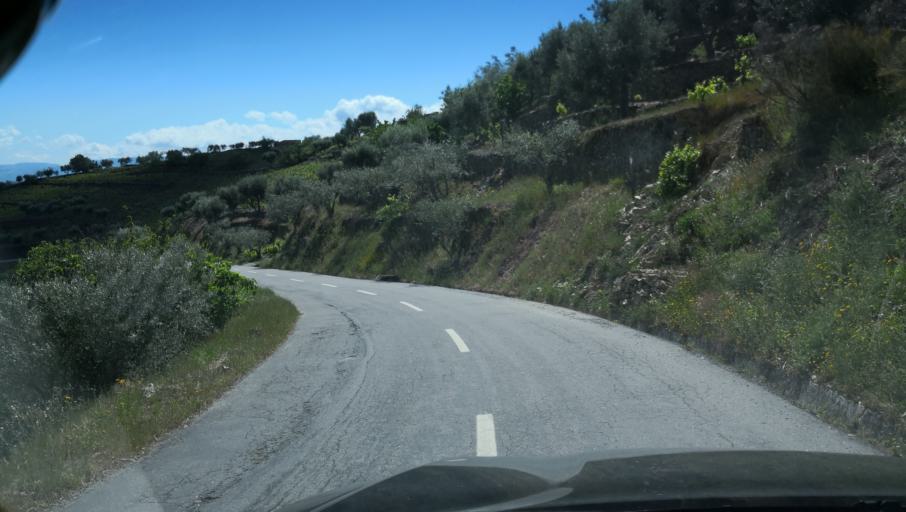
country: PT
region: Vila Real
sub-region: Vila Real
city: Vila Real
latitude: 41.2501
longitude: -7.7371
